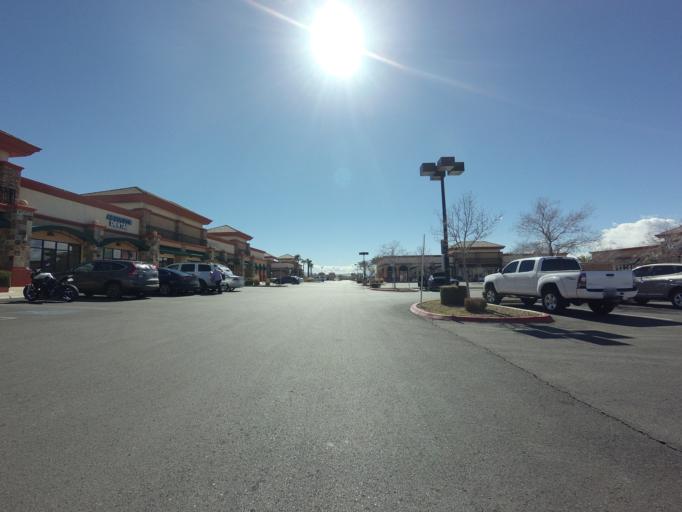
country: US
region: Nevada
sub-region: Clark County
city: Nellis Air Force Base
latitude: 36.2671
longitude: -115.1158
